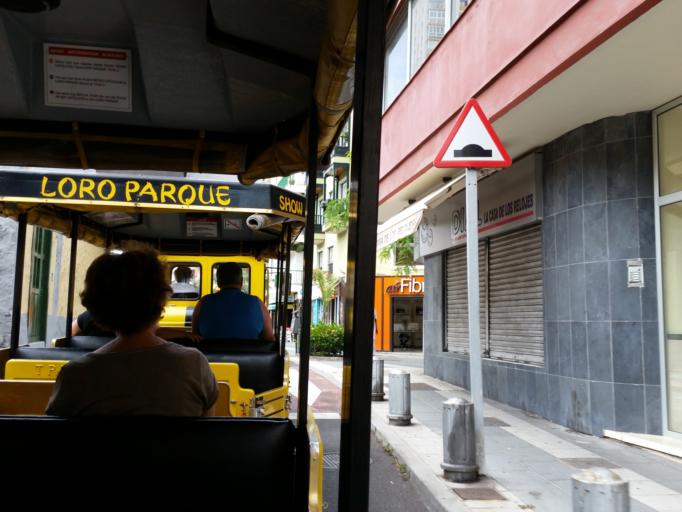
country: ES
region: Canary Islands
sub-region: Provincia de Santa Cruz de Tenerife
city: Puerto de la Cruz
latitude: 28.4153
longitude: -16.5464
